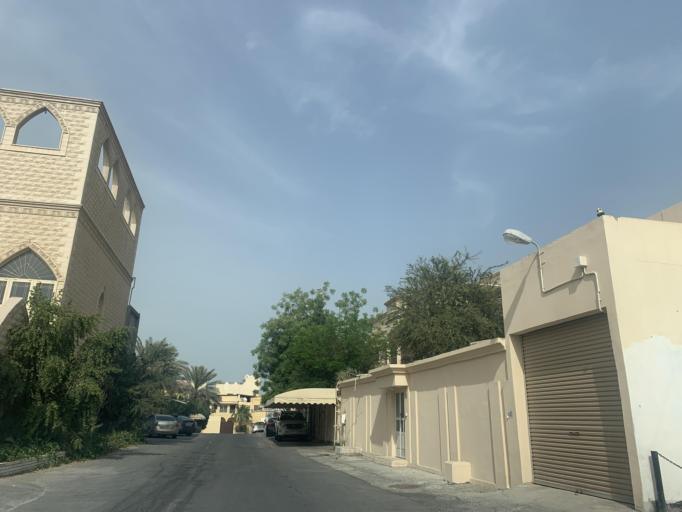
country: BH
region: Northern
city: Ar Rifa'
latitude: 26.1309
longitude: 50.5556
